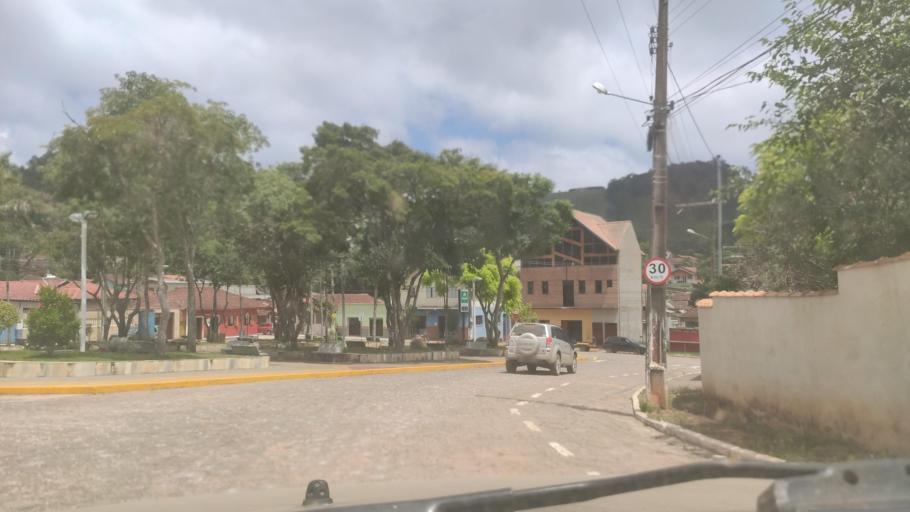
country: BR
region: Minas Gerais
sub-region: Cambui
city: Cambui
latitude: -22.6583
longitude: -45.9171
